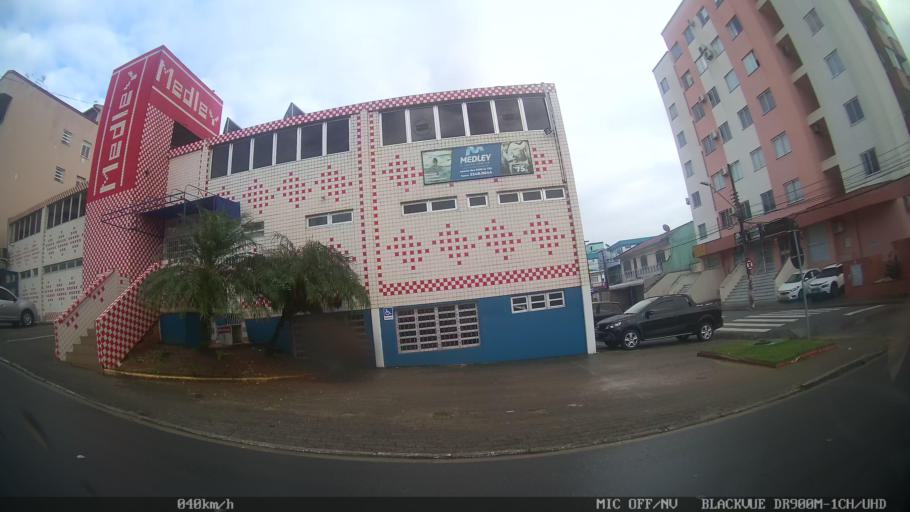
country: BR
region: Santa Catarina
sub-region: Sao Jose
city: Campinas
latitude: -27.5738
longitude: -48.6043
